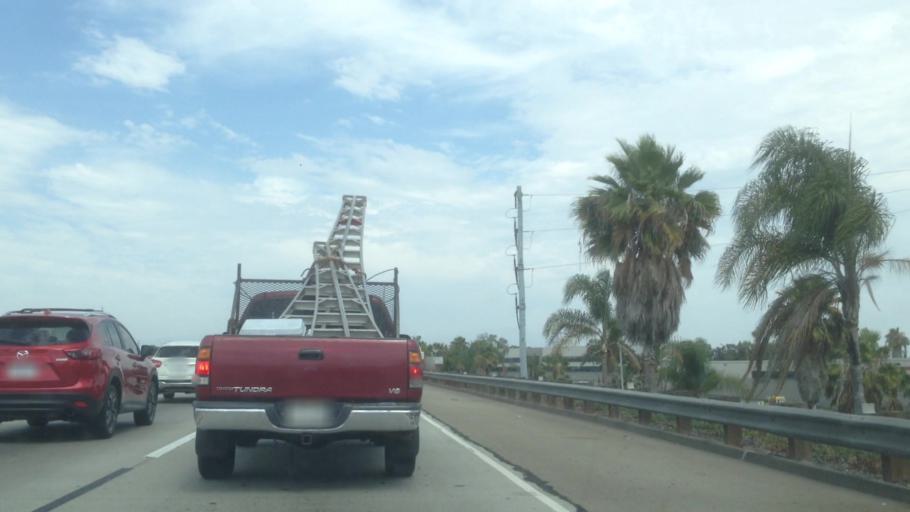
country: US
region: California
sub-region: Orange County
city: Garden Grove
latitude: 33.7724
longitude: -117.9251
